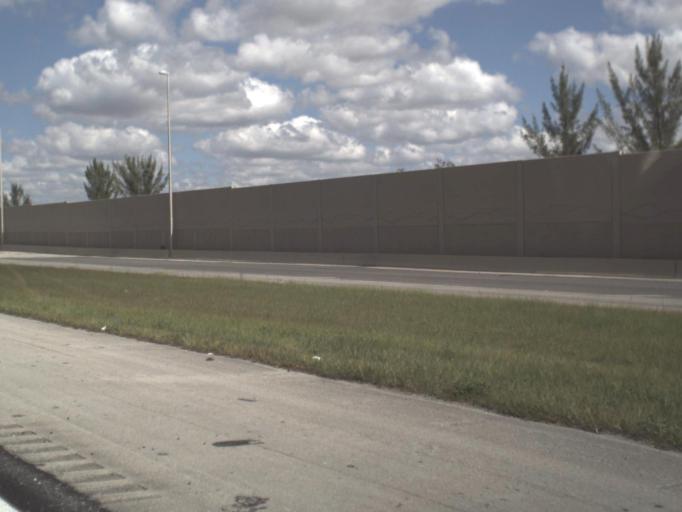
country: US
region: Florida
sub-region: Miami-Dade County
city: Doral
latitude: 25.8475
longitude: -80.3872
